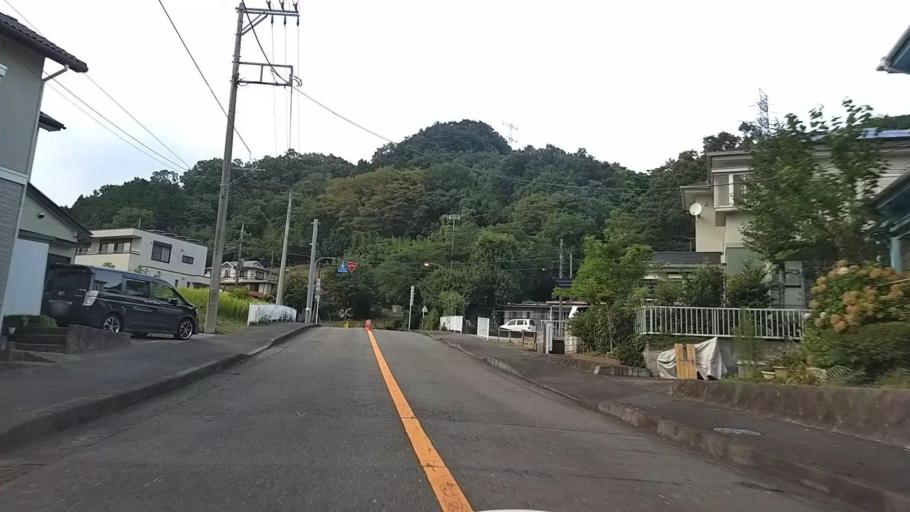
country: JP
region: Yamanashi
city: Uenohara
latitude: 35.6126
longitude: 139.2163
